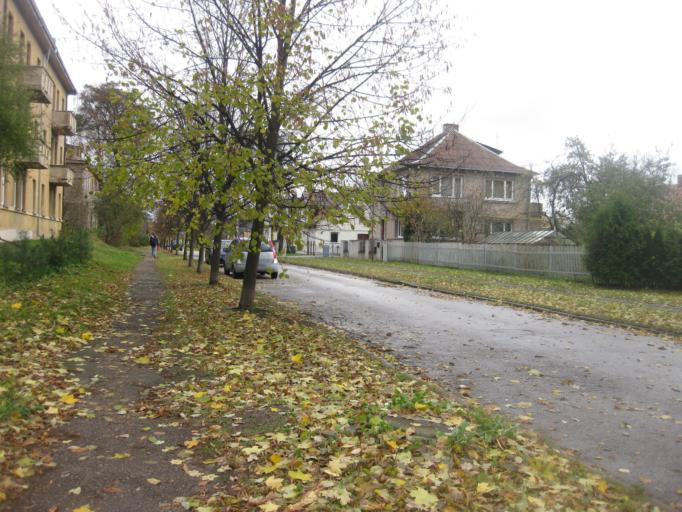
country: LT
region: Kauno apskritis
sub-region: Kaunas
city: Eiguliai
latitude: 54.9056
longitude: 23.9331
